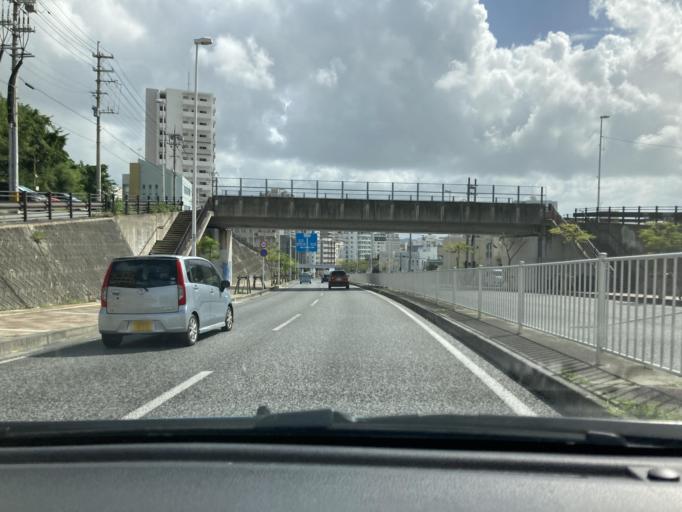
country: JP
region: Okinawa
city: Naha-shi
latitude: 26.2233
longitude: 127.6925
